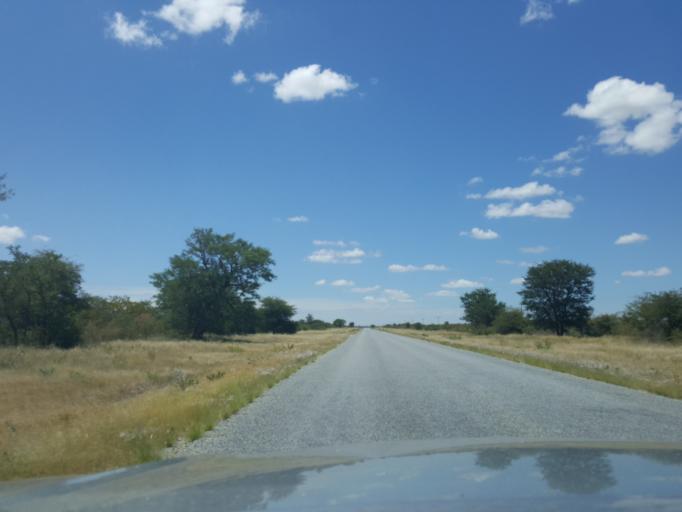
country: BW
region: Central
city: Gweta
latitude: -20.1354
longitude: 25.6557
